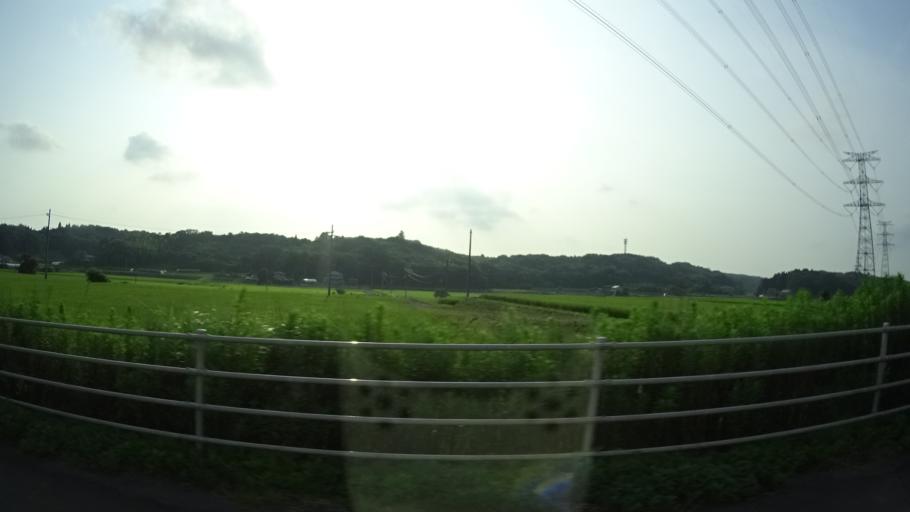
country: JP
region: Tochigi
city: Motegi
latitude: 36.5584
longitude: 140.1026
